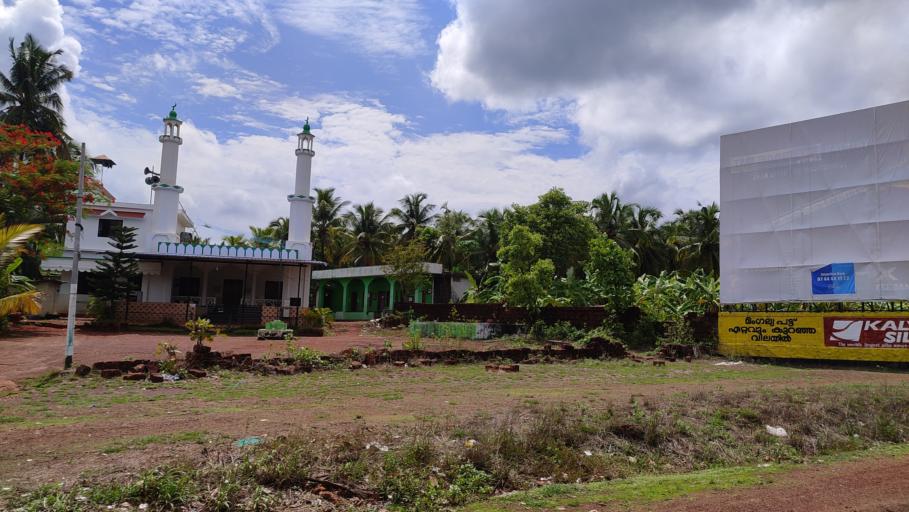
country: IN
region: Kerala
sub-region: Kasaragod District
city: Kannangad
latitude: 12.3843
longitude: 75.1009
